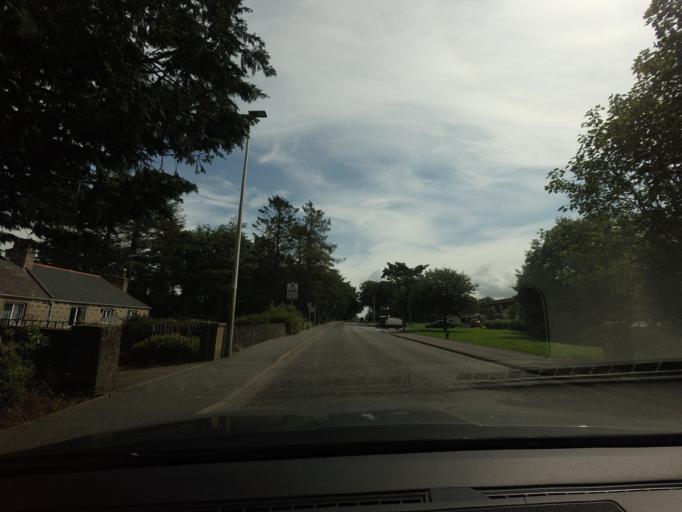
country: GB
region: Scotland
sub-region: Aberdeenshire
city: Mintlaw
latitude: 57.5253
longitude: -2.0094
